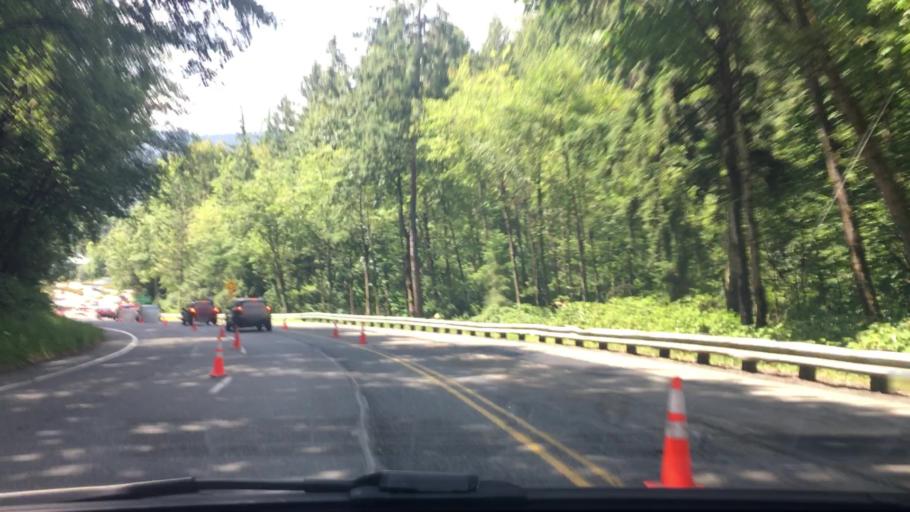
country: US
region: Washington
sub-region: King County
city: City of Sammamish
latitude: 47.5705
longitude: -122.0525
